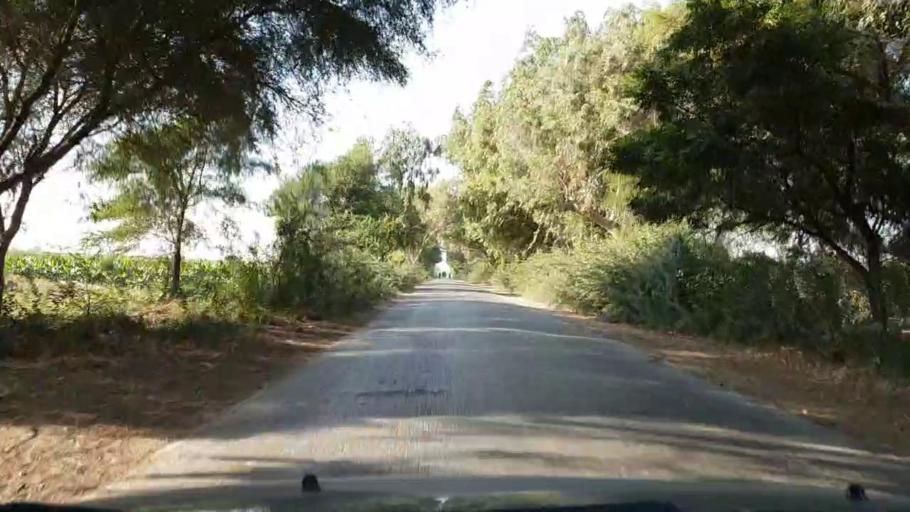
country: PK
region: Sindh
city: Tando Ghulam Ali
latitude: 25.1355
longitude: 68.8786
